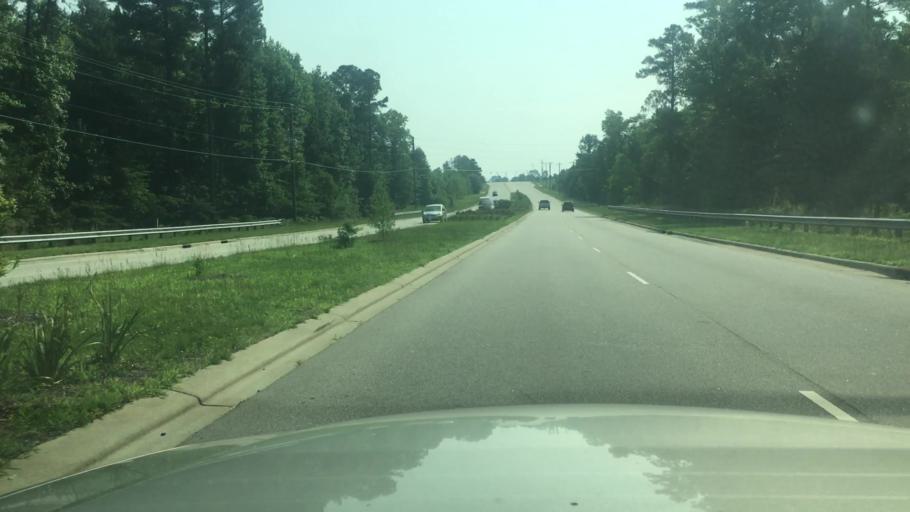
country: US
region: North Carolina
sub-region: Cumberland County
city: Hope Mills
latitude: 34.9884
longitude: -78.9548
